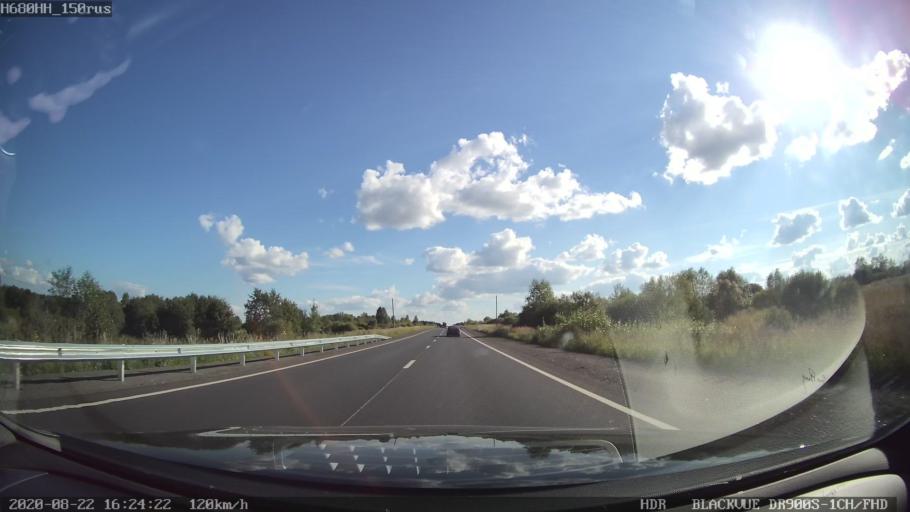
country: RU
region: Tverskaya
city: Rameshki
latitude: 57.3385
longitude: 36.0956
